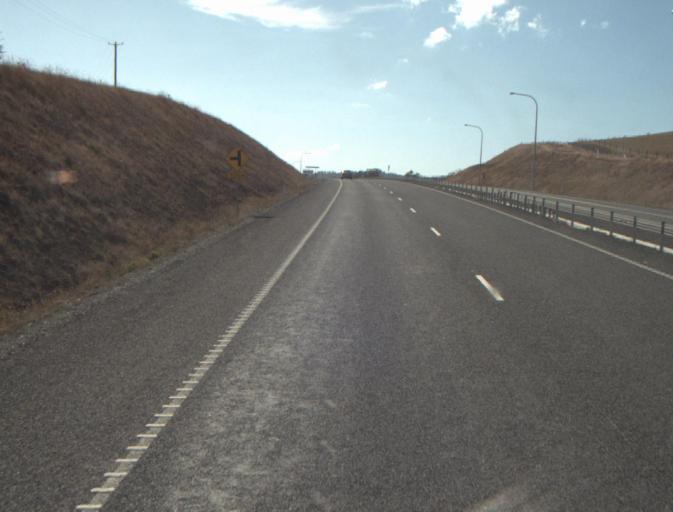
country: AU
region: Tasmania
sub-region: Launceston
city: Mayfield
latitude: -41.3578
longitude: 147.1057
